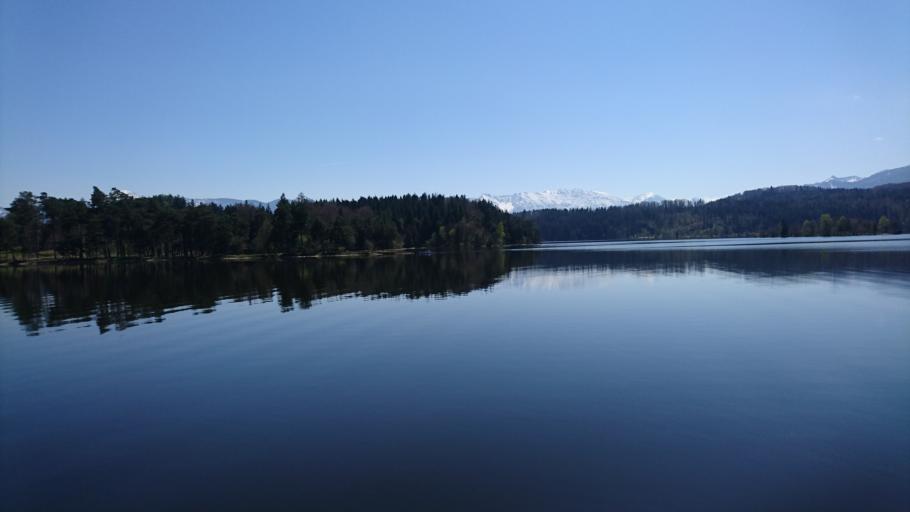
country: DE
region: Bavaria
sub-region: Upper Bavaria
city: Uffing
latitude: 47.6883
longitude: 11.1572
